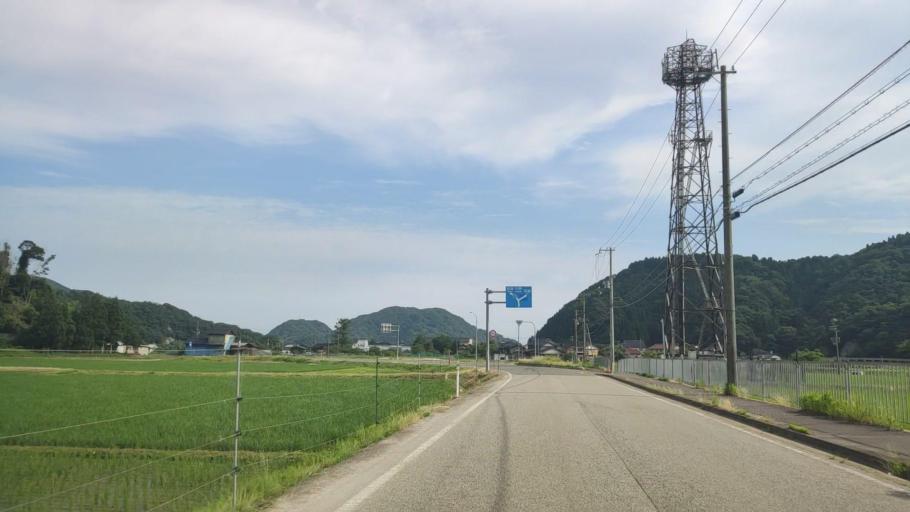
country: JP
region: Hyogo
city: Toyooka
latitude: 35.6314
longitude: 134.8409
